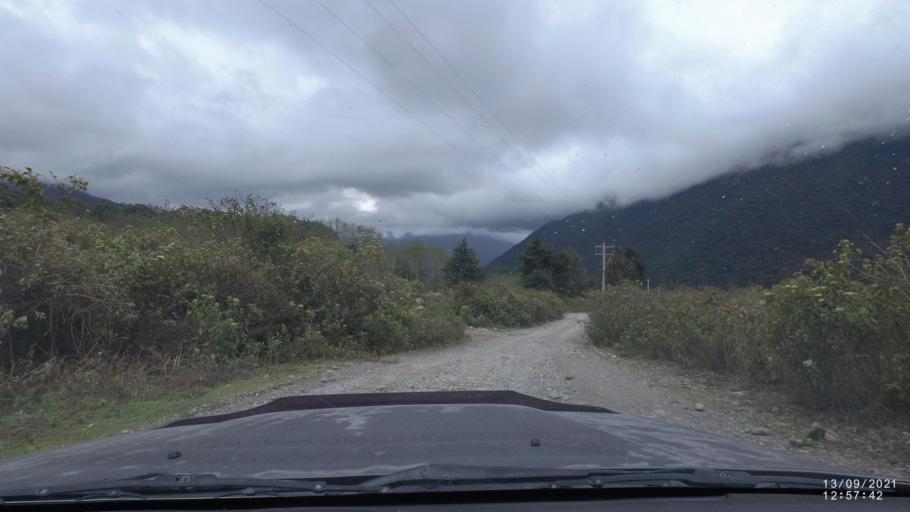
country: BO
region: Cochabamba
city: Colomi
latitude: -17.2400
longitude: -65.8179
